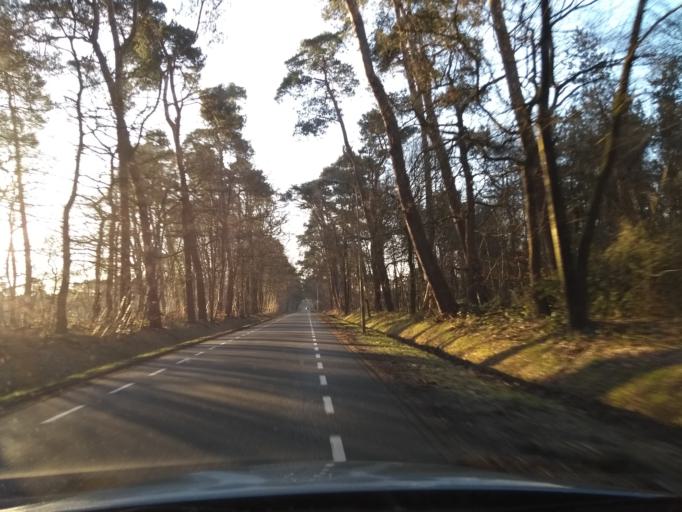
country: NL
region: Overijssel
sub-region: Gemeente Hof van Twente
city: Delden
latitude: 52.2440
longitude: 6.7252
